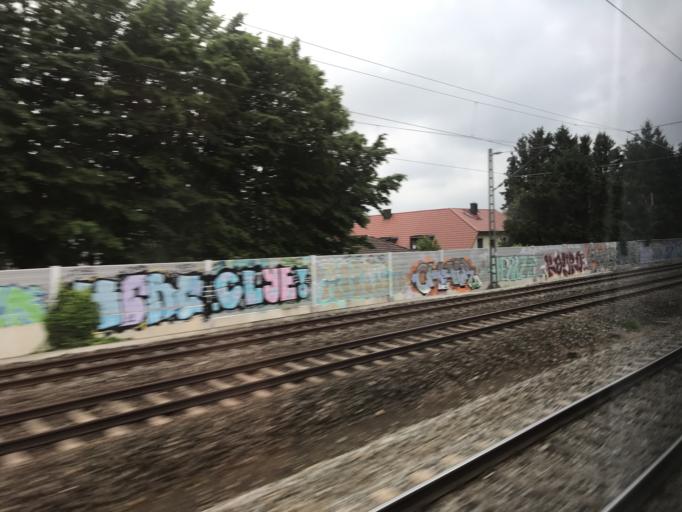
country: DE
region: Bavaria
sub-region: Upper Bavaria
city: Grobenzell
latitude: 48.1814
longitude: 11.3995
